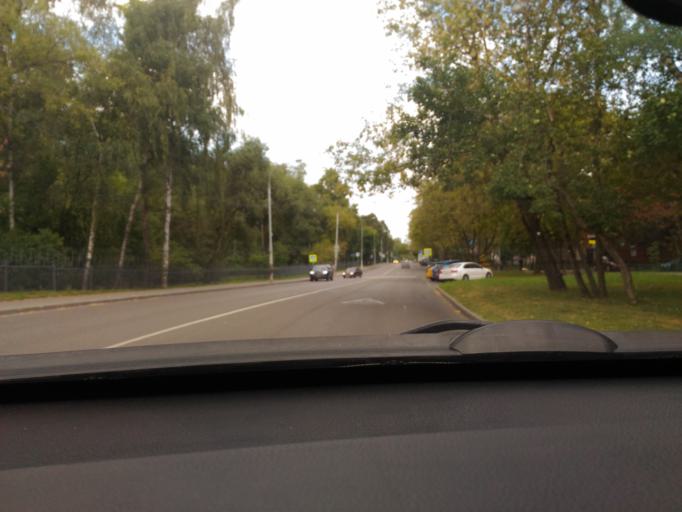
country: RU
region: Moscow
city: Vatutino
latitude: 55.8873
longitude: 37.6912
